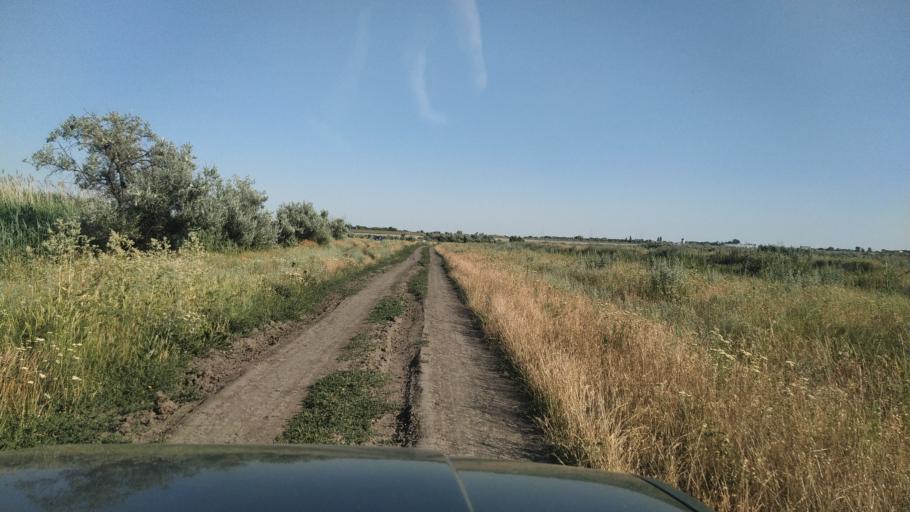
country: RU
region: Rostov
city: Kuleshovka
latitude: 47.1228
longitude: 39.6482
